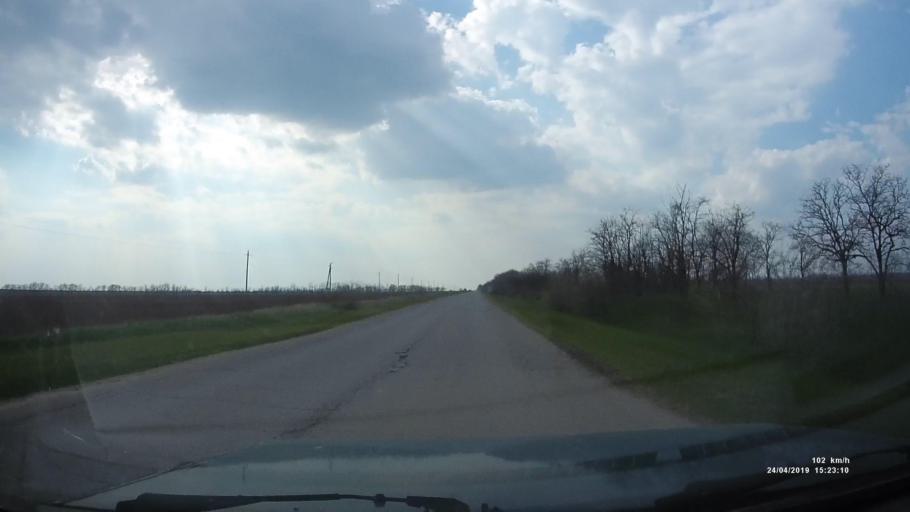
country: RU
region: Rostov
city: Remontnoye
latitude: 46.5421
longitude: 43.0954
